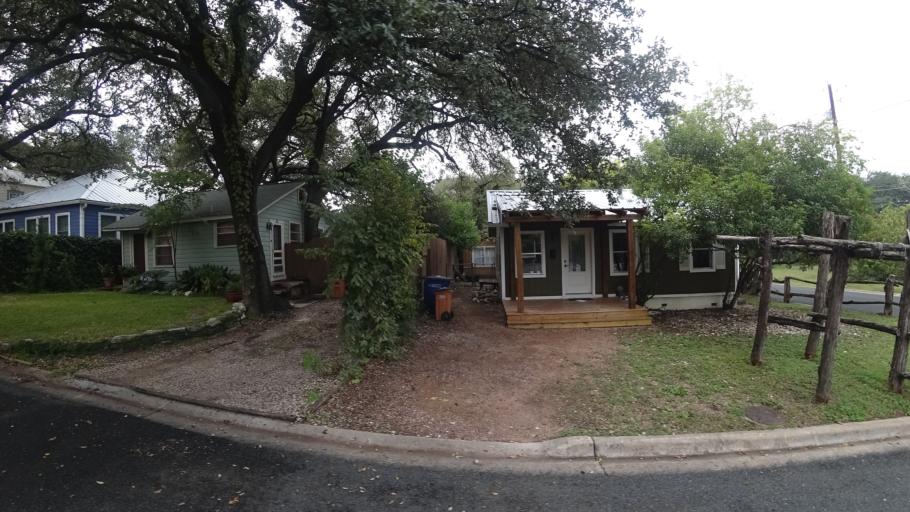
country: US
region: Texas
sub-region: Travis County
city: Austin
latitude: 30.2528
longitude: -97.7590
